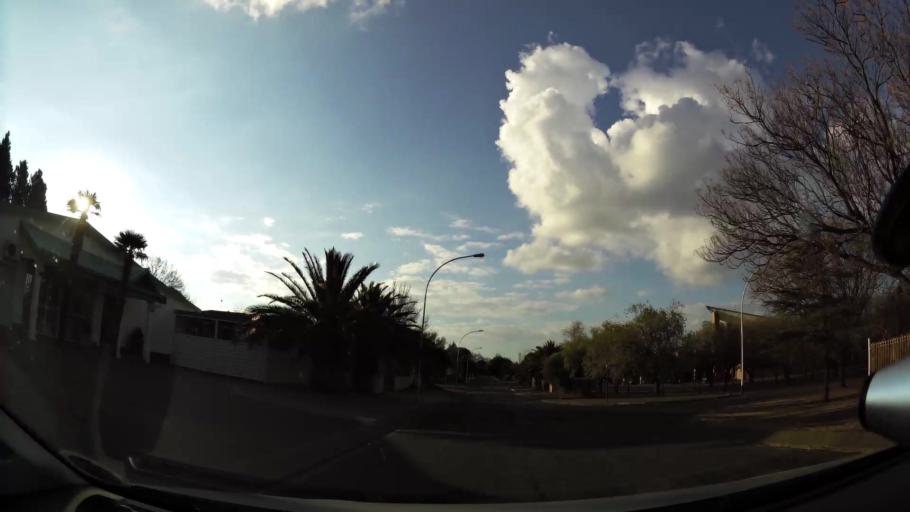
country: ZA
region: Orange Free State
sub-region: Mangaung Metropolitan Municipality
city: Bloemfontein
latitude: -29.1483
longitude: 26.1807
